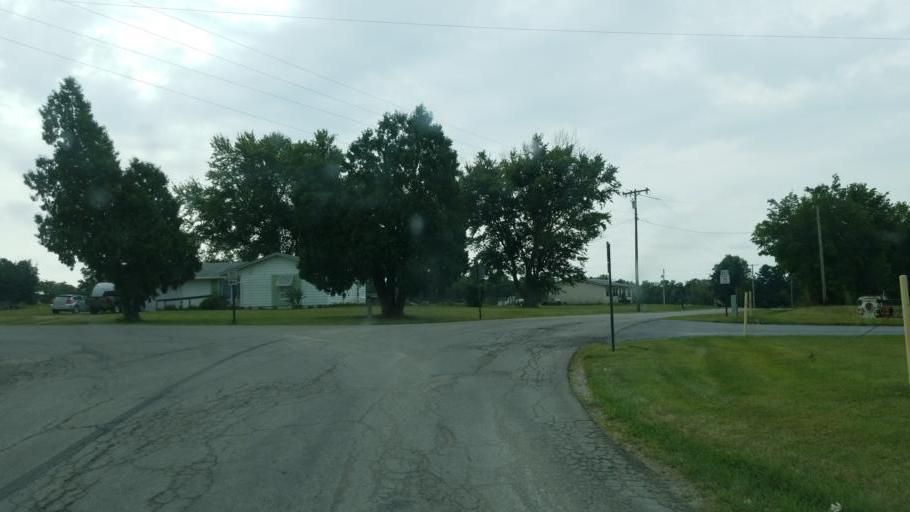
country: US
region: Ohio
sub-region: Crawford County
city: Galion
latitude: 40.6620
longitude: -82.8385
